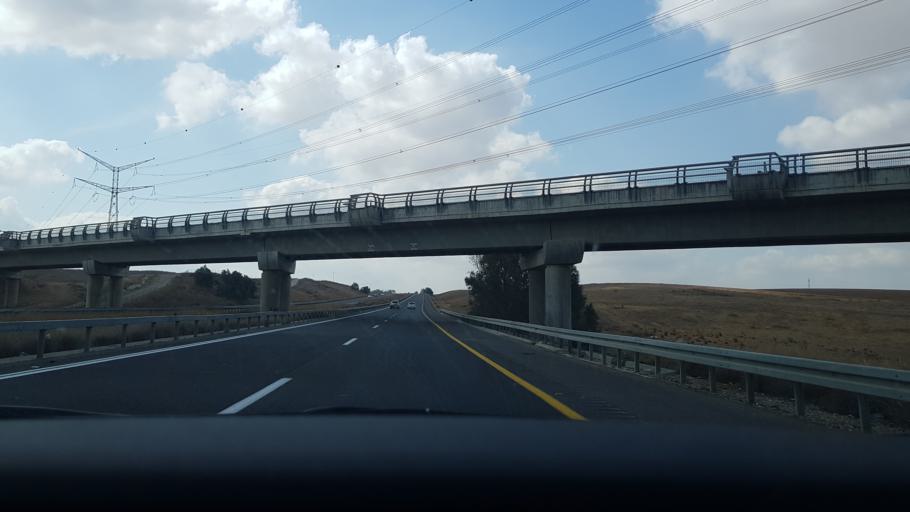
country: IL
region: Southern District
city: Qiryat Gat
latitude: 31.5261
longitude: 34.7888
